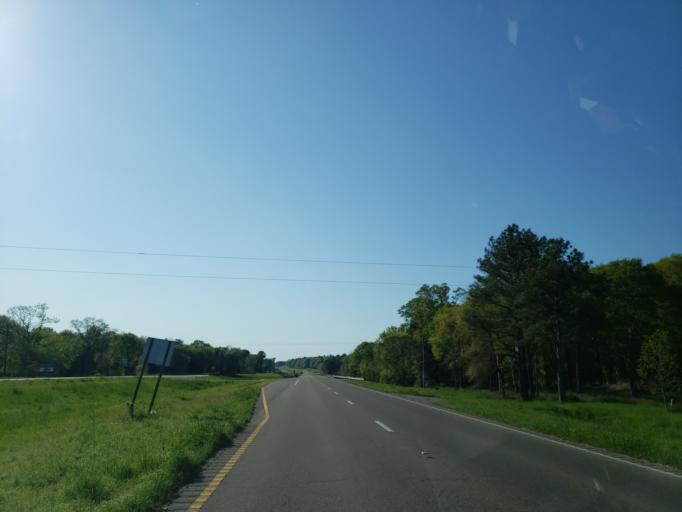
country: US
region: Mississippi
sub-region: Jones County
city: Ellisville
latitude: 31.6800
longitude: -89.3060
